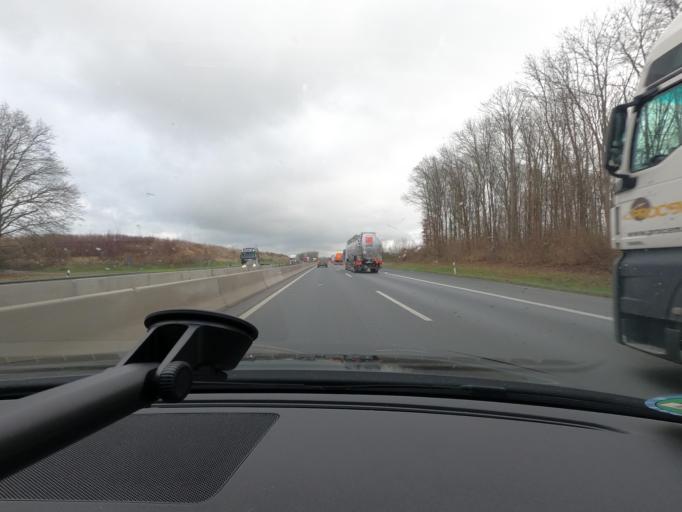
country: DE
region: North Rhine-Westphalia
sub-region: Regierungsbezirk Arnsberg
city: Werl
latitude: 51.5358
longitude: 7.9157
